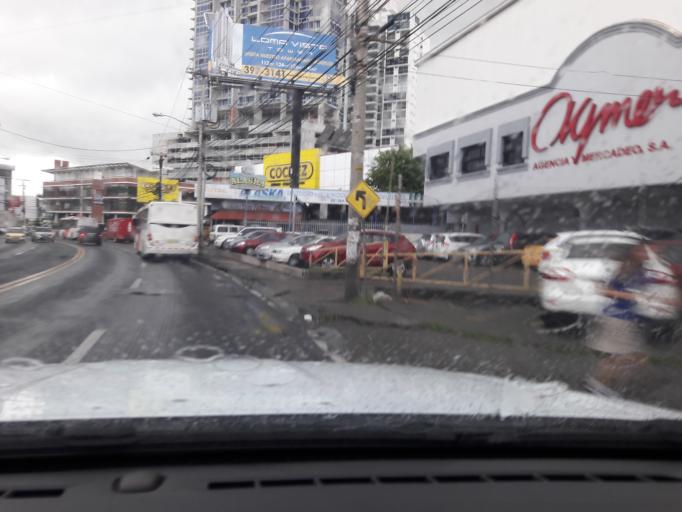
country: PA
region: Panama
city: Panama
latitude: 9.0045
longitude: -79.5142
